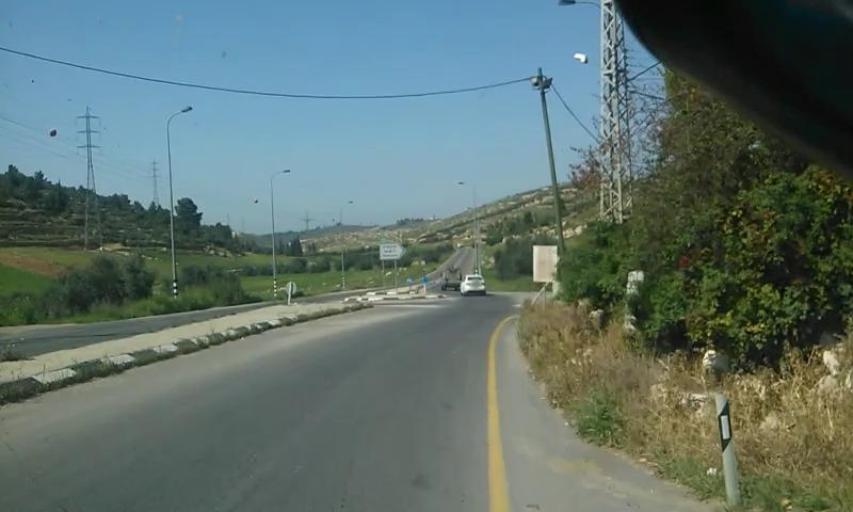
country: PS
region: West Bank
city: Idhna
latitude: 31.5749
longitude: 34.9817
